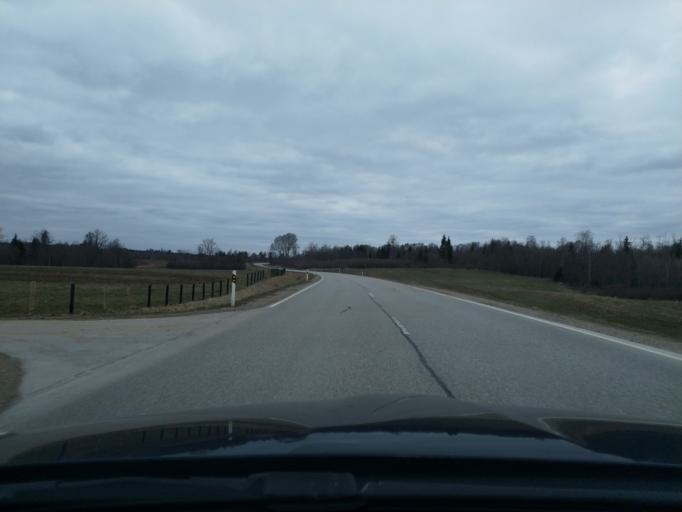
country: LV
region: Kuldigas Rajons
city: Kuldiga
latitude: 56.9610
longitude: 22.0890
